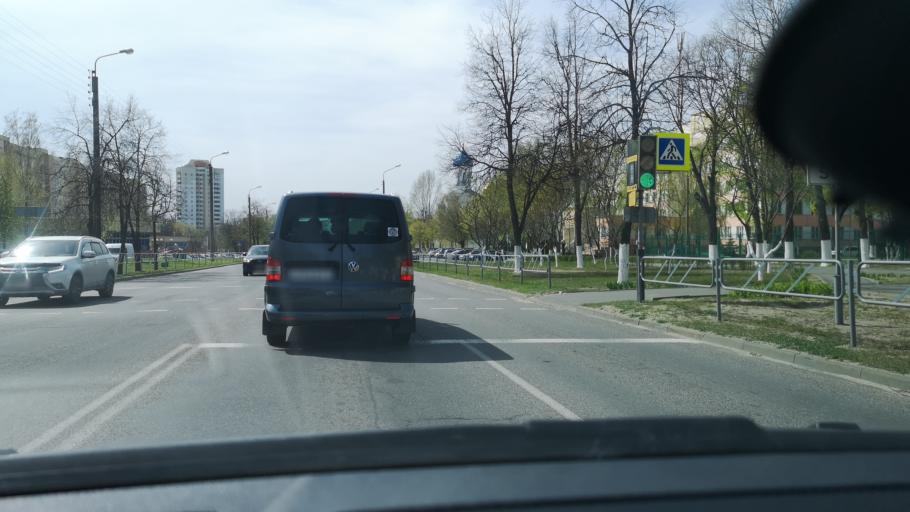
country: BY
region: Gomel
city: Gomel
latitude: 52.4126
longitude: 30.9768
